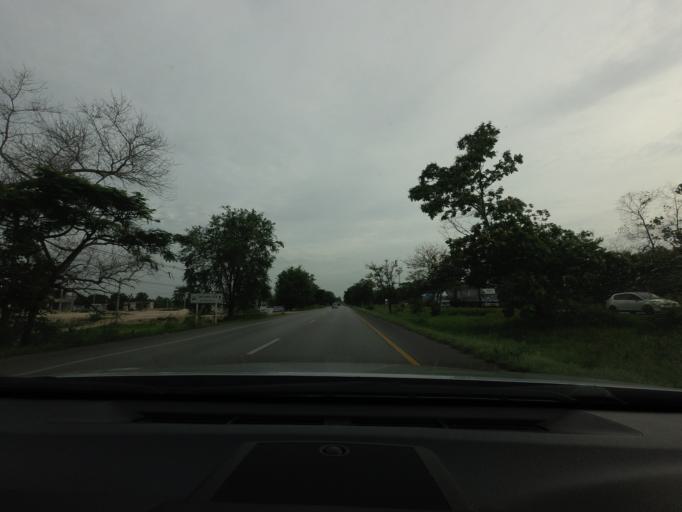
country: TH
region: Phetchaburi
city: Cha-am
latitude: 12.7260
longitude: 99.9253
